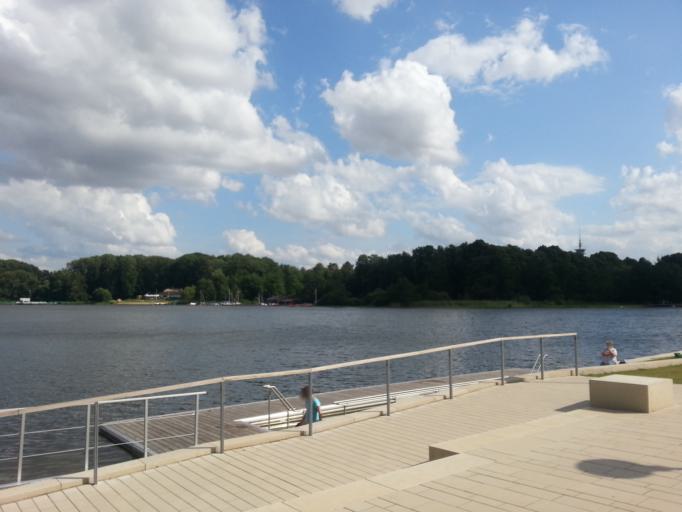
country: DE
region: Schleswig-Holstein
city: Bad Segeberg
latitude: 53.9430
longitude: 10.3116
